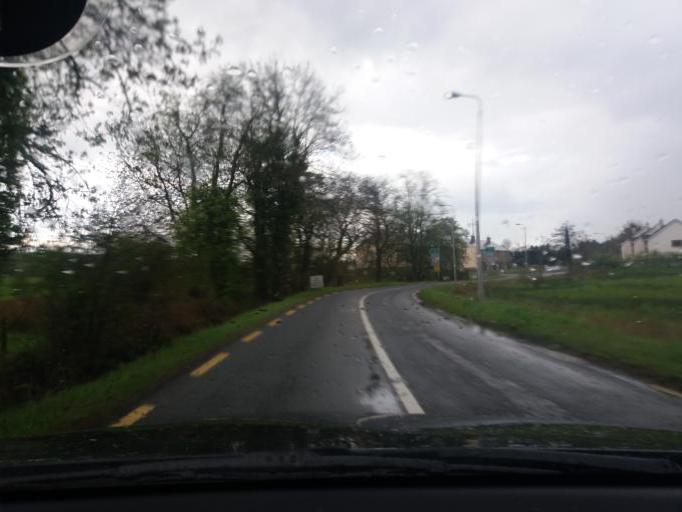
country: IE
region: Ulster
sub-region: An Cabhan
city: Ballyconnell
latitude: 54.1247
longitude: -7.6793
